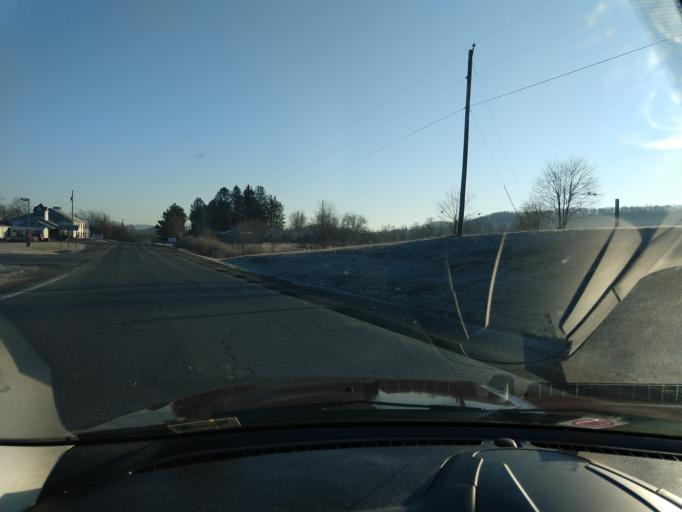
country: US
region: West Virginia
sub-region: Greenbrier County
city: Rainelle
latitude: 37.8529
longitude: -80.7204
